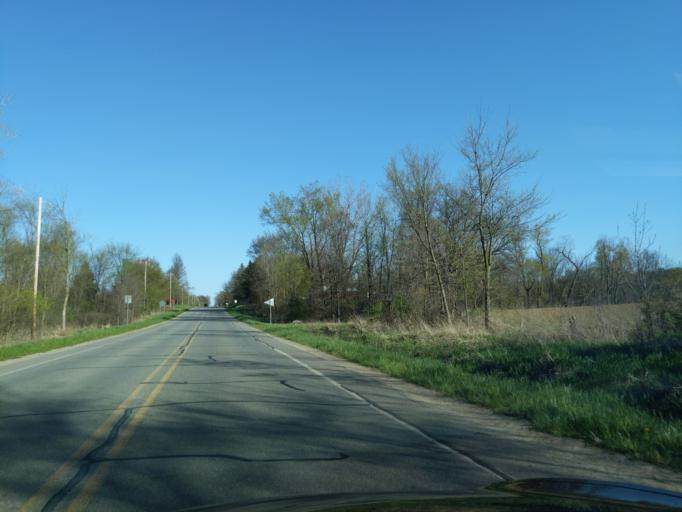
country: US
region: Michigan
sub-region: Ionia County
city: Portland
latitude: 42.8485
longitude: -84.8746
